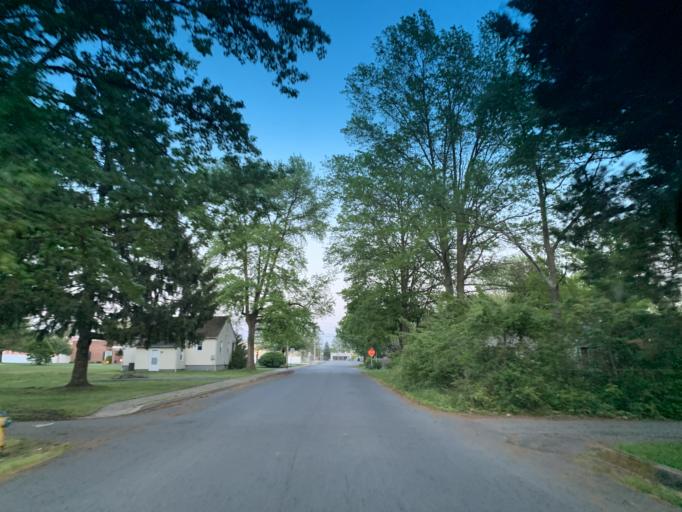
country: US
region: Maryland
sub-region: Harford County
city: Aberdeen
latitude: 39.5048
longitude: -76.1697
